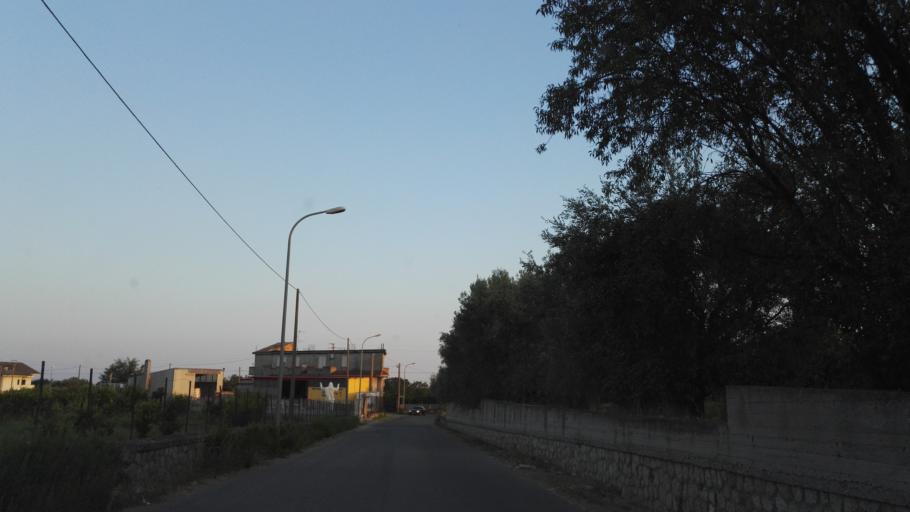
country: IT
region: Calabria
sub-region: Provincia di Reggio Calabria
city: Caulonia Marina
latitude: 38.3615
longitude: 16.4690
